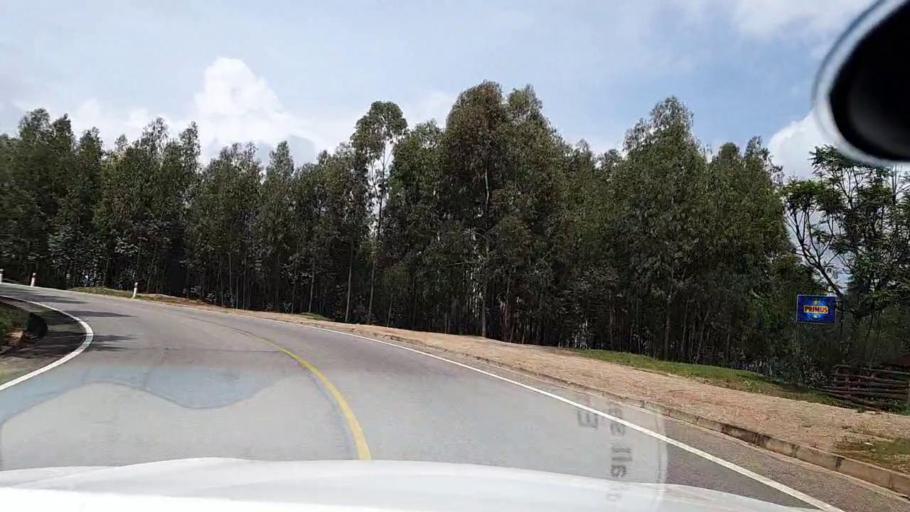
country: RW
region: Southern Province
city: Nzega
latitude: -2.4927
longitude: 29.5073
